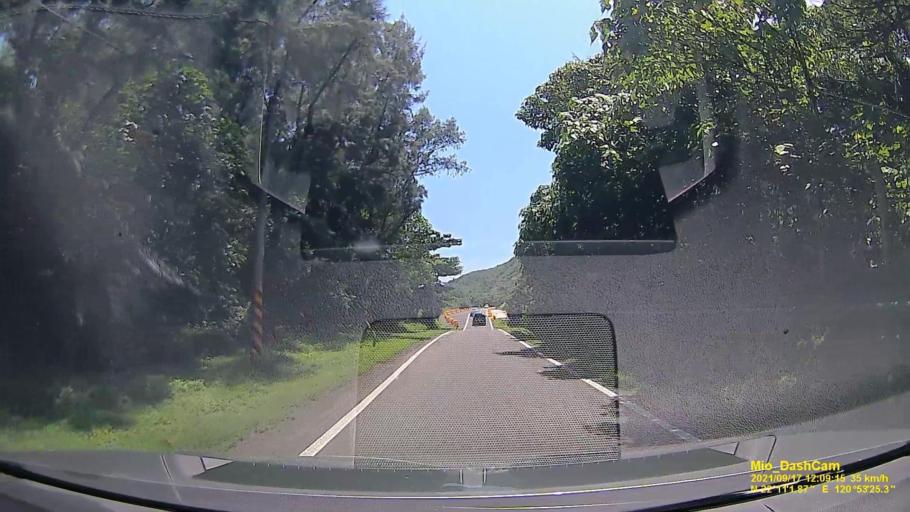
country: TW
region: Taiwan
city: Hengchun
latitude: 22.1839
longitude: 120.8903
